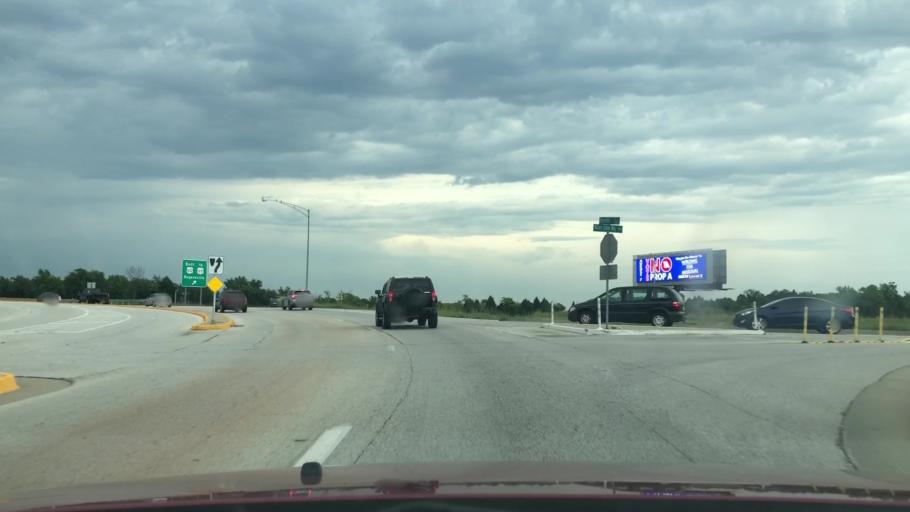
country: US
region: Missouri
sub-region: Greene County
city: Springfield
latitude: 37.1378
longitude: -93.2536
